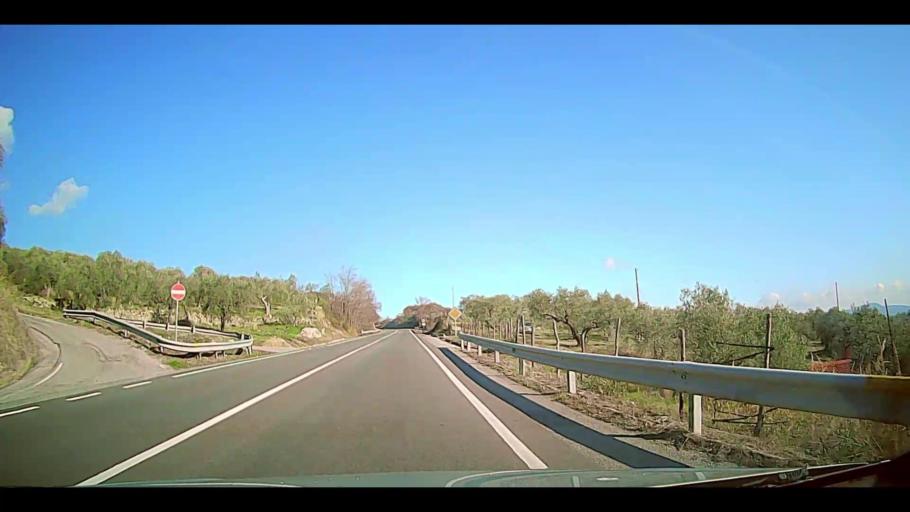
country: IT
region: Calabria
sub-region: Provincia di Crotone
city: Caccuri
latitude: 39.2127
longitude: 16.7966
